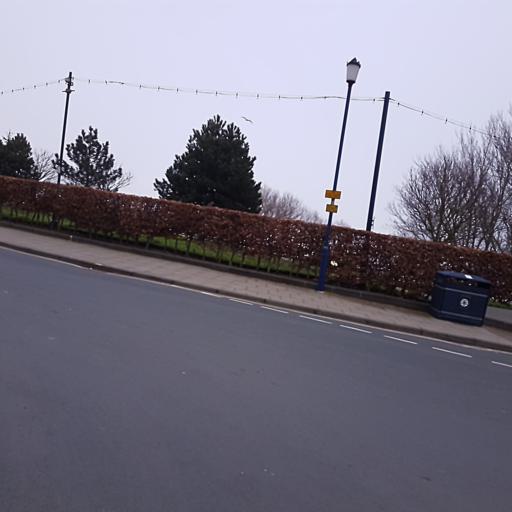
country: GB
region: England
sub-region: North Yorkshire
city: Filey
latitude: 54.2064
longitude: -0.2867
